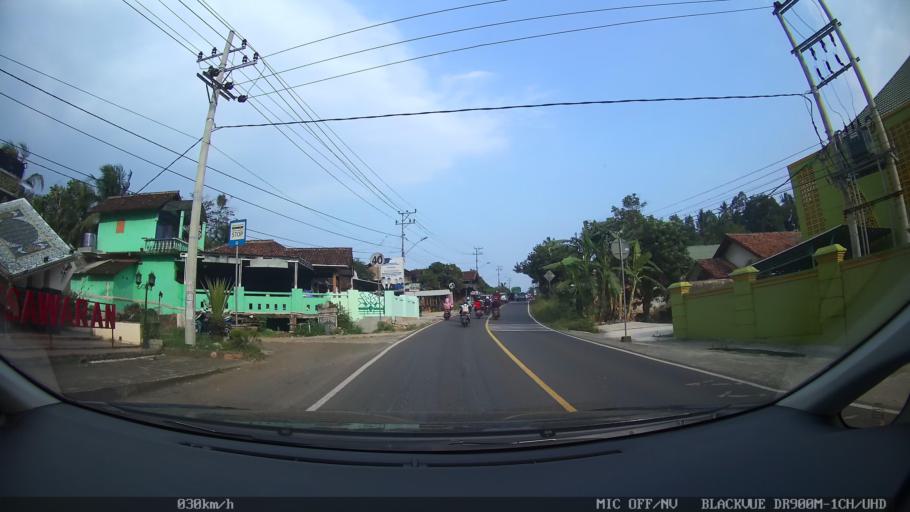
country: ID
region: Lampung
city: Natar
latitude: -5.3668
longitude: 105.1693
